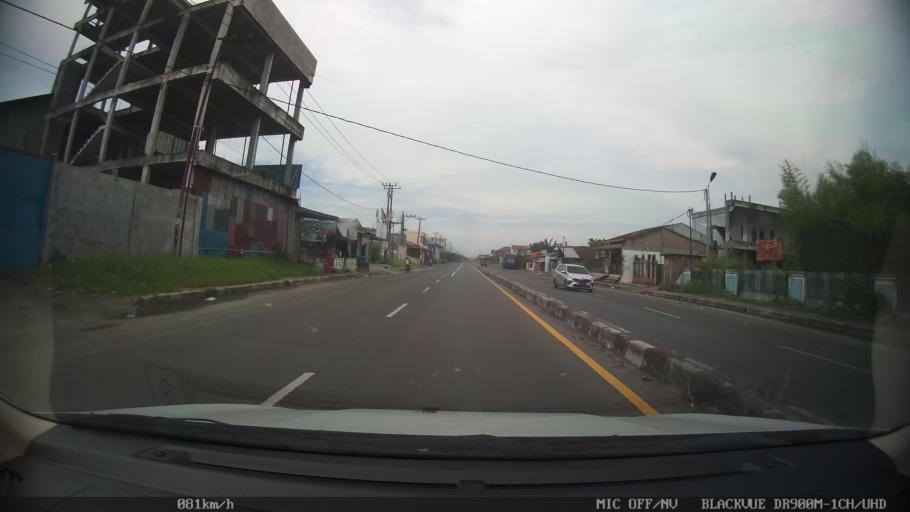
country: ID
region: North Sumatra
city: Sunggal
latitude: 3.6127
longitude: 98.5759
